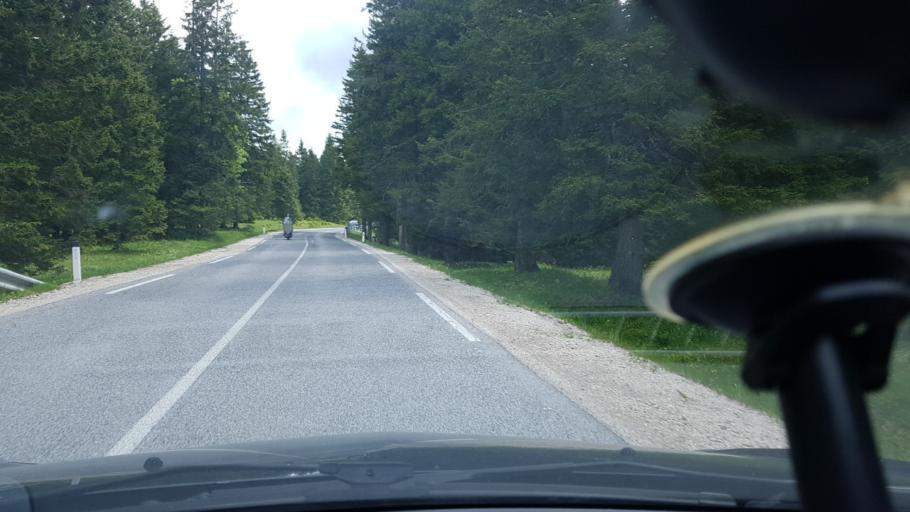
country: SI
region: Mislinja
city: Mislinja
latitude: 46.4498
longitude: 15.3210
